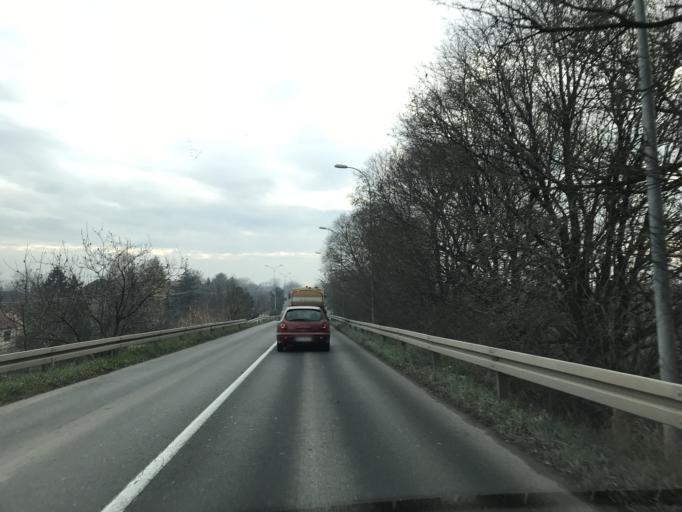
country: RS
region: Autonomna Pokrajina Vojvodina
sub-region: Sremski Okrug
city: Ingija
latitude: 45.0351
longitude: 20.0949
